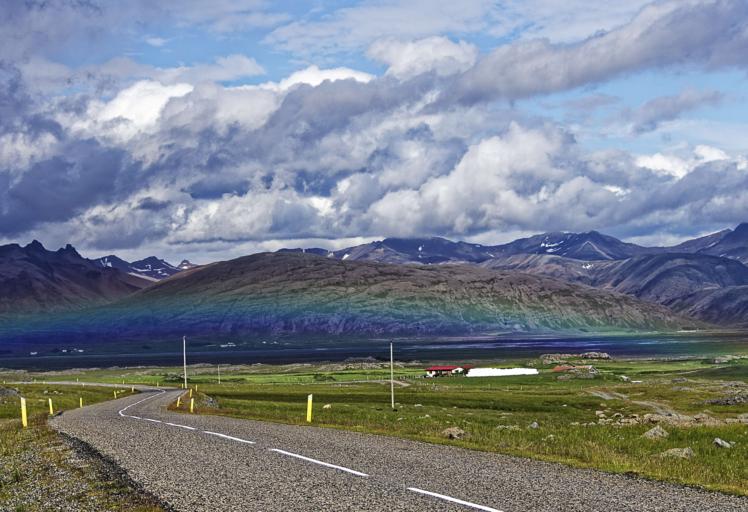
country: IS
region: East
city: Hoefn
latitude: 64.3459
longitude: -14.9268
